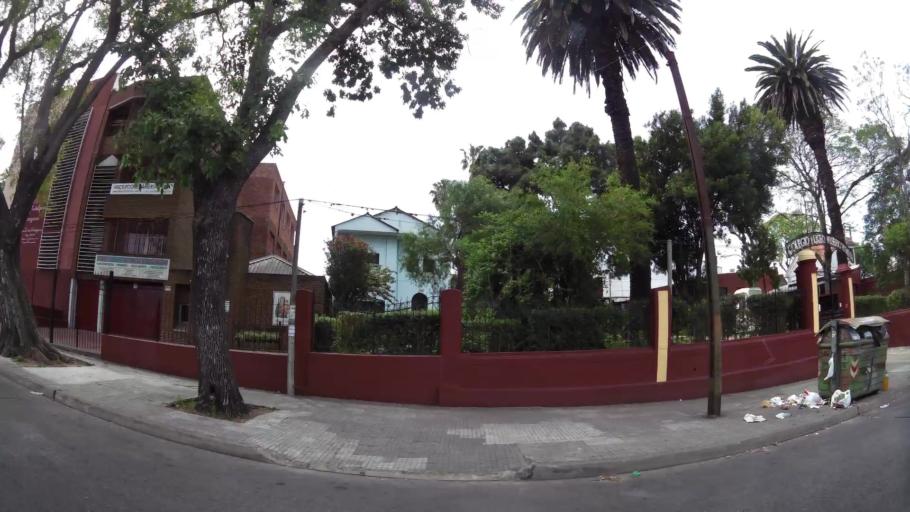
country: UY
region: Montevideo
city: Montevideo
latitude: -34.8553
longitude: -56.1735
